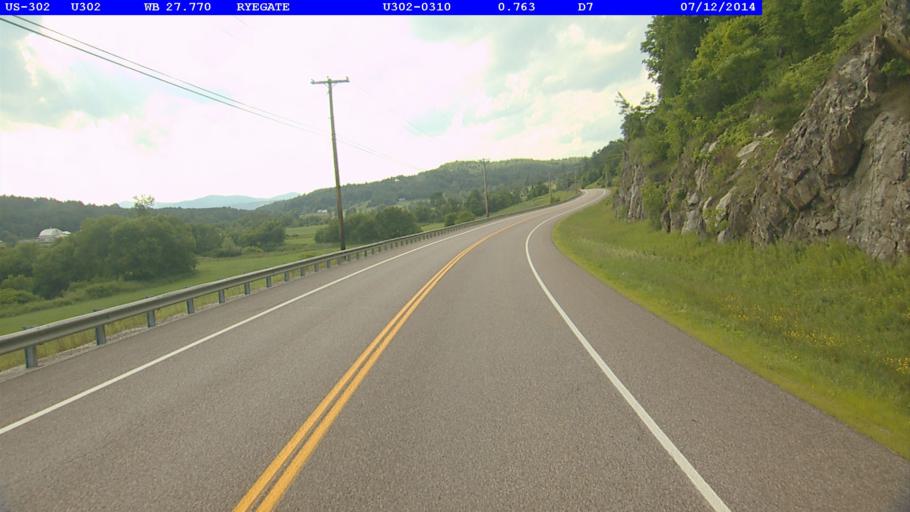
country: US
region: New Hampshire
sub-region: Grafton County
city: Woodsville
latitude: 44.1985
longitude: -72.1592
